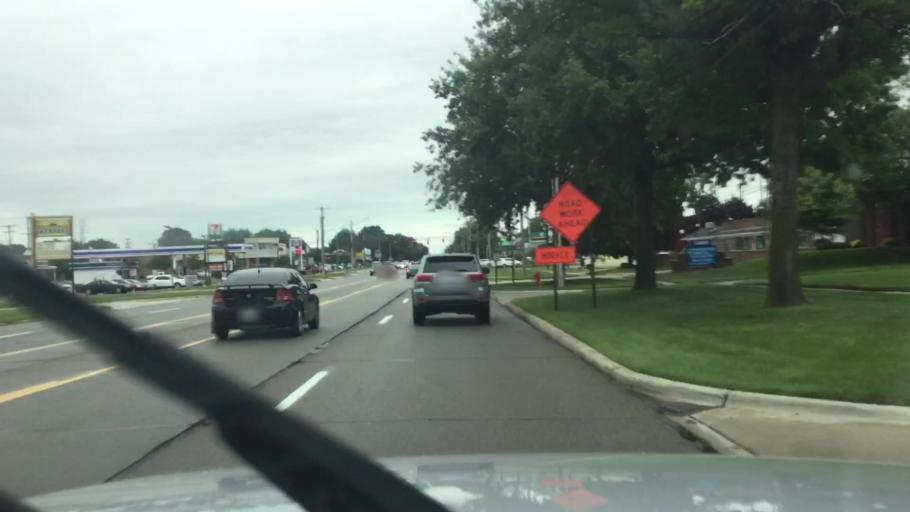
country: US
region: Michigan
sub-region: Macomb County
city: Center Line
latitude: 42.5213
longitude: -83.0100
